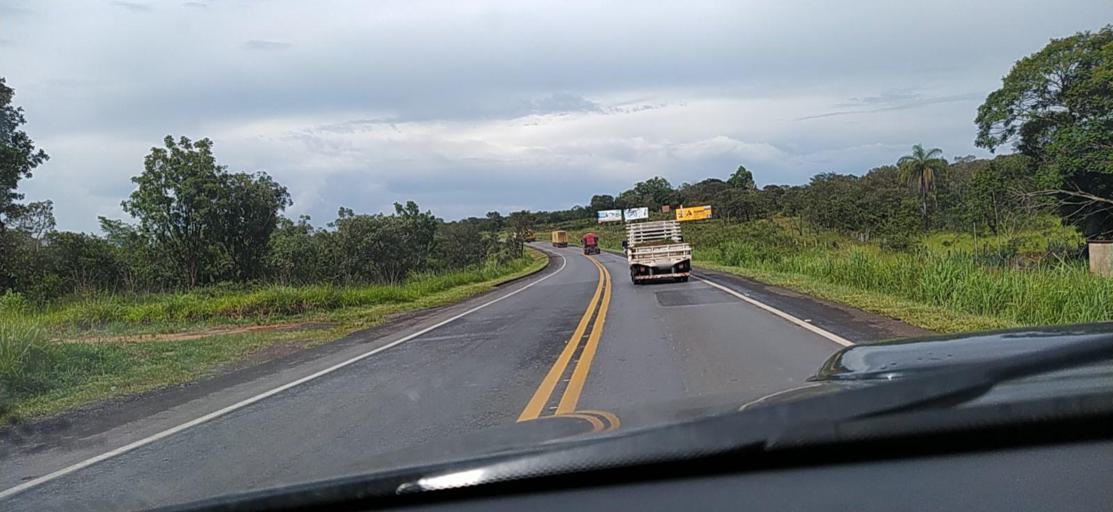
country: BR
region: Minas Gerais
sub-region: Montes Claros
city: Montes Claros
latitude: -16.8712
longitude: -43.8558
